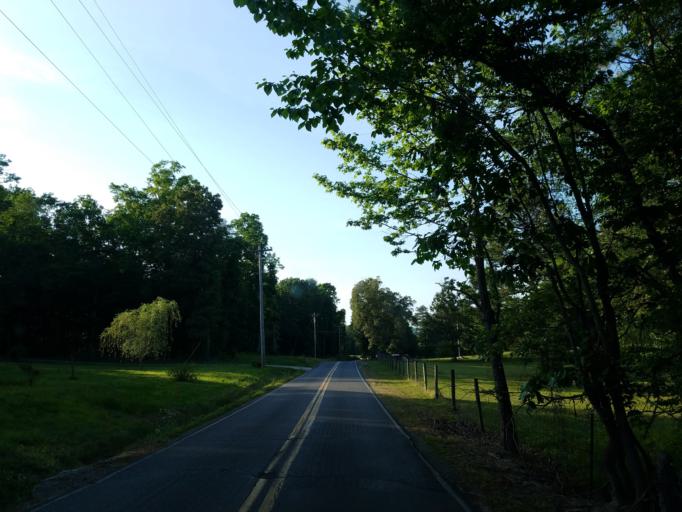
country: US
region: Georgia
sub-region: Gordon County
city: Calhoun
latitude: 34.4977
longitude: -85.1146
